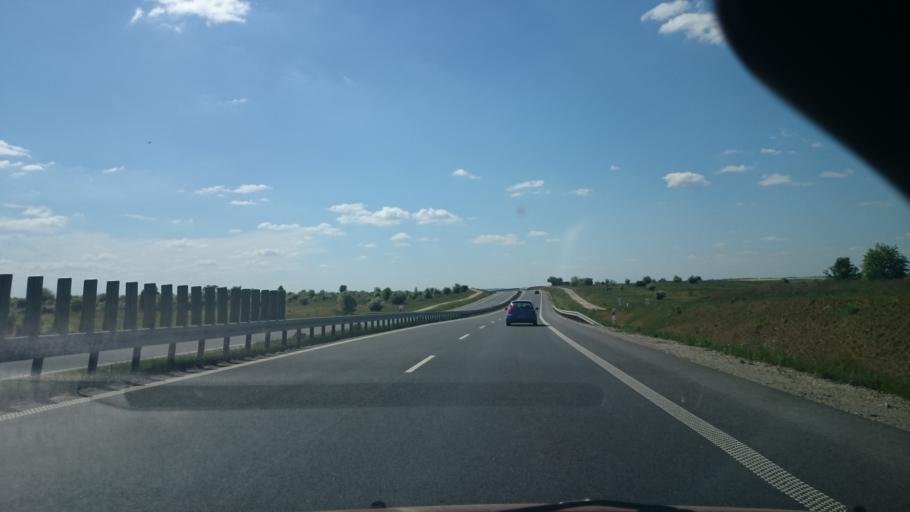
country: PL
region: Opole Voivodeship
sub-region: Powiat nyski
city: Nysa
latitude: 50.5005
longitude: 17.3140
